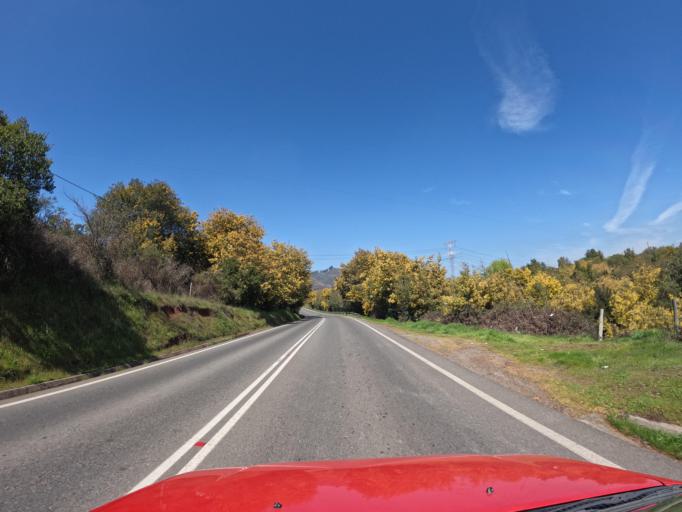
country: CL
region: Maule
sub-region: Provincia de Talca
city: San Clemente
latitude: -35.4727
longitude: -71.2751
